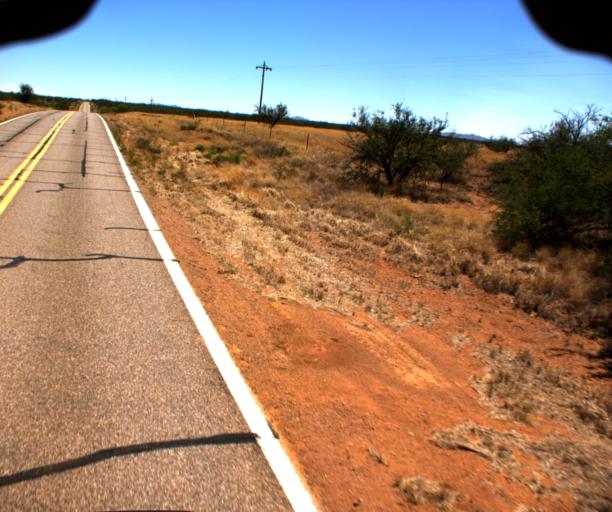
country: US
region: Arizona
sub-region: Pima County
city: Three Points
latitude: 31.7445
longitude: -111.4831
